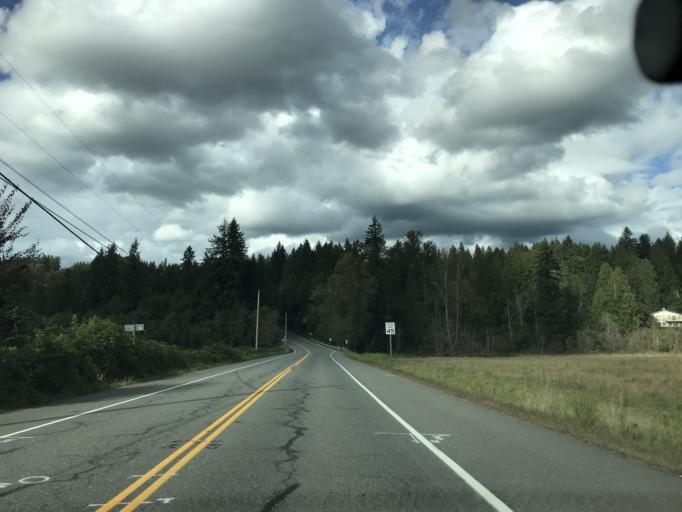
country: US
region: Washington
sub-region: King County
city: Black Diamond
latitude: 47.2841
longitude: -122.0529
